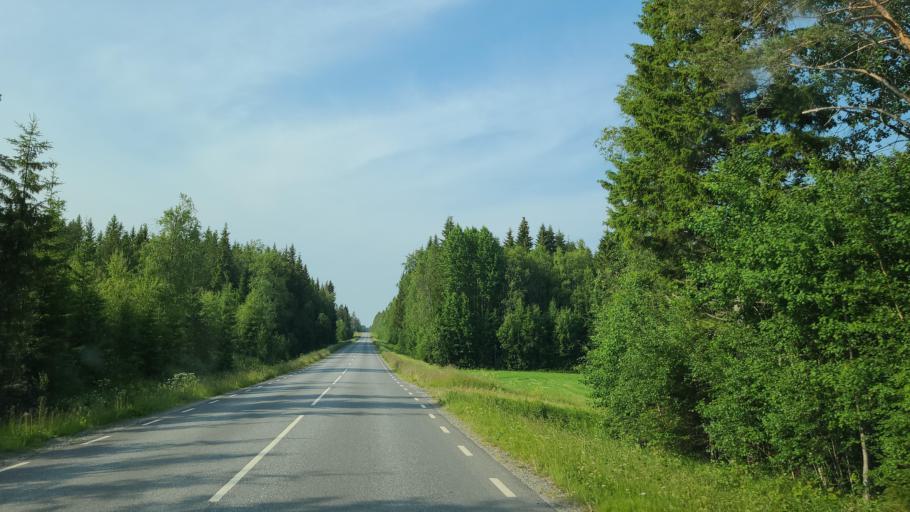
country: SE
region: Vaesterbotten
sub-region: Skelleftea Kommun
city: Burea
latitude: 64.4253
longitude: 21.3532
